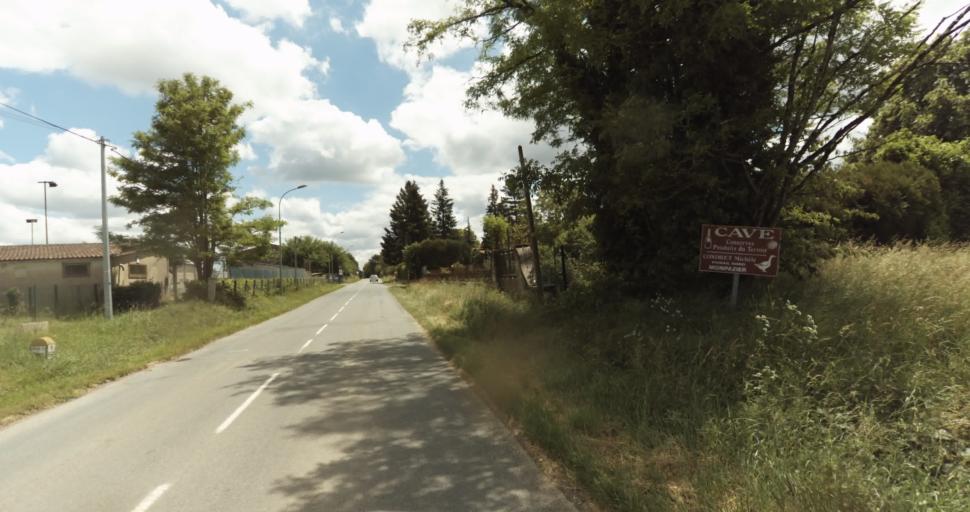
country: FR
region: Aquitaine
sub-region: Departement de la Dordogne
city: Beaumont-du-Perigord
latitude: 44.6880
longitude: 0.8868
